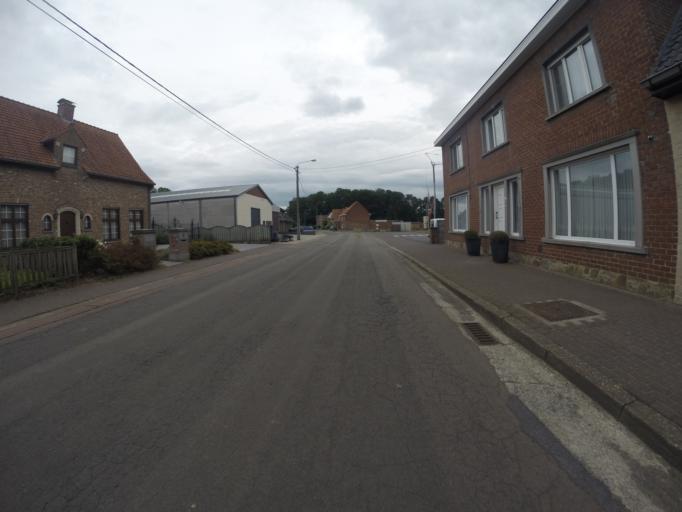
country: BE
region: Flanders
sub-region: Provincie West-Vlaanderen
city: Ruiselede
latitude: 51.0746
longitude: 3.3537
